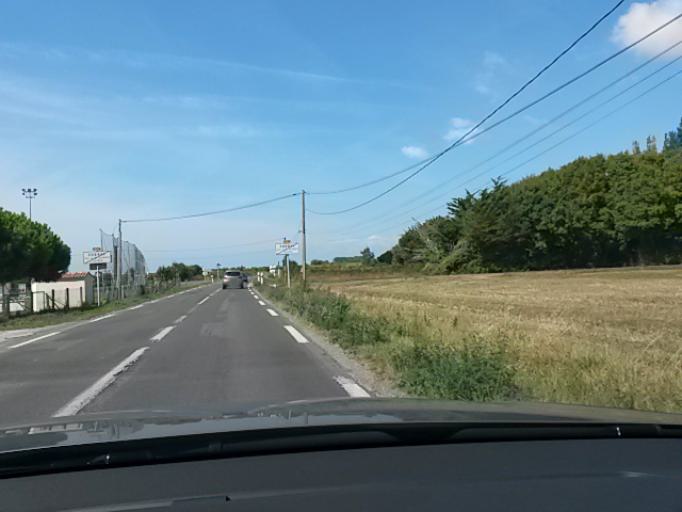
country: FR
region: Poitou-Charentes
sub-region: Departement de la Charente-Maritime
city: Saint-Denis-d'Oleron
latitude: 45.9787
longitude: -1.3550
